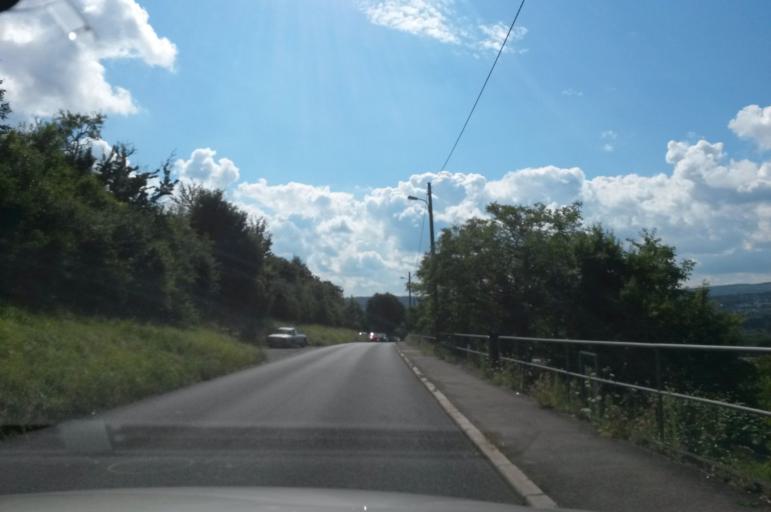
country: DE
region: Baden-Wuerttemberg
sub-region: Karlsruhe Region
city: Ispringen
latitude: 48.8961
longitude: 8.6608
